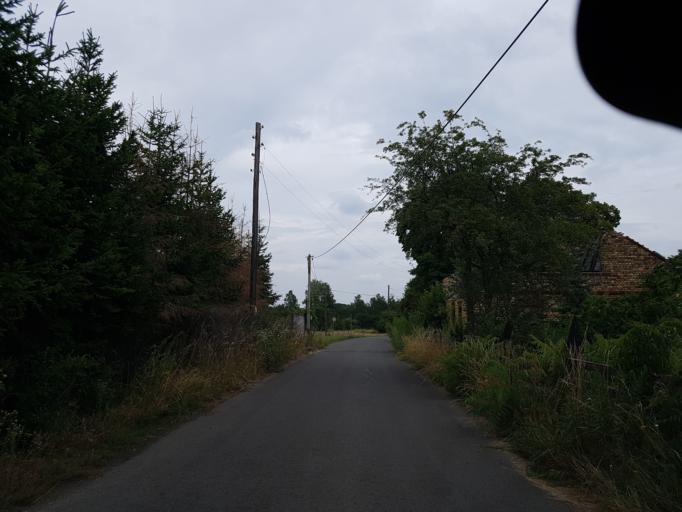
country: DE
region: Brandenburg
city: Schipkau
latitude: 51.5563
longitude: 13.8859
